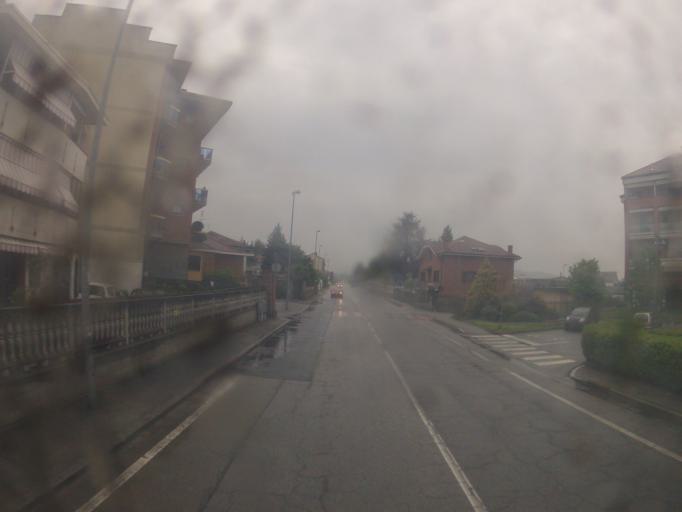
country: IT
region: Piedmont
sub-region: Provincia di Torino
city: La Loggia
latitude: 44.9592
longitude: 7.6675
